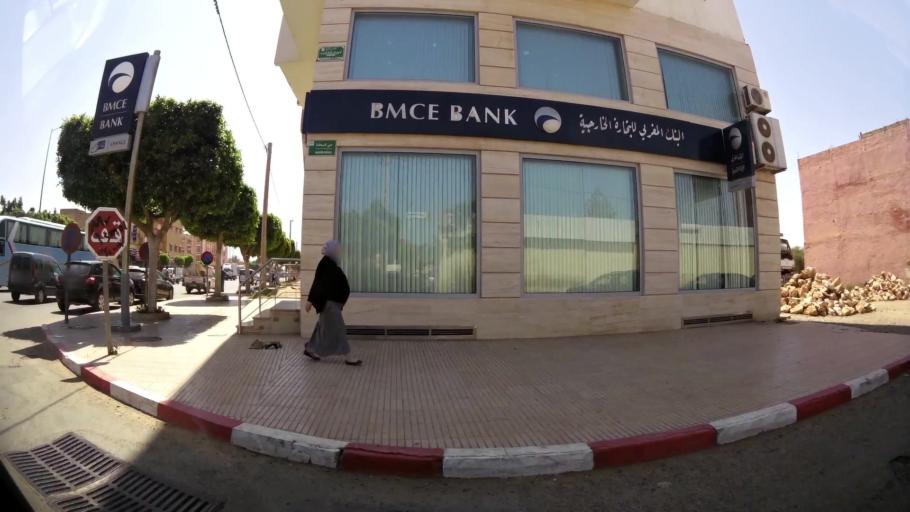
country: MA
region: Souss-Massa-Draa
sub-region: Inezgane-Ait Mellou
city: Inezgane
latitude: 30.3394
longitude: -9.4958
